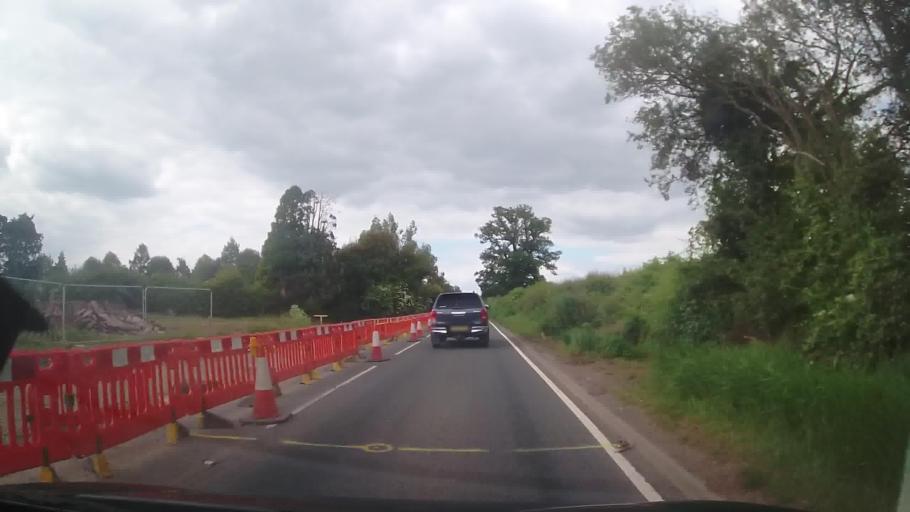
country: GB
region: England
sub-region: Herefordshire
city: Hereford
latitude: 52.0804
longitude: -2.7220
